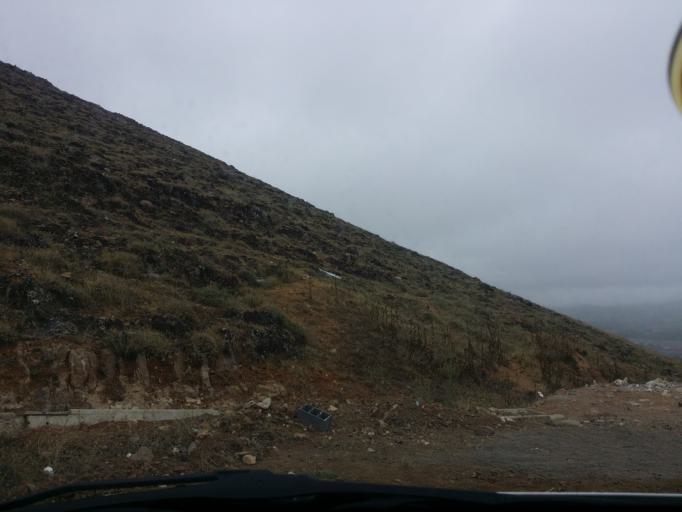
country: IR
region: Mazandaran
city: `Abbasabad
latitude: 36.5103
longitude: 51.1531
